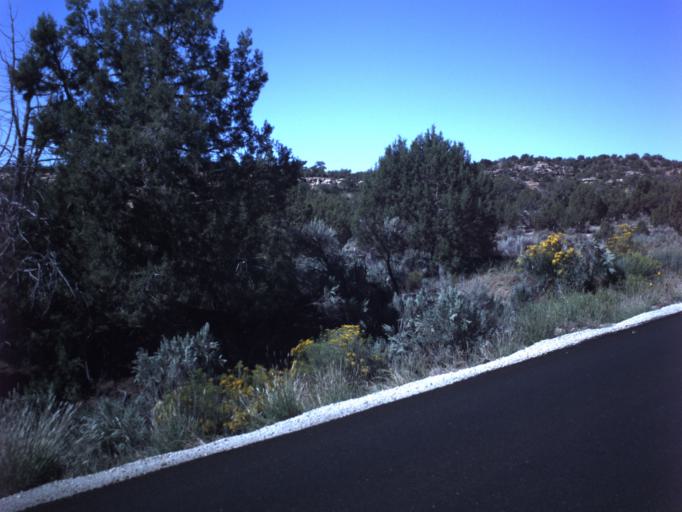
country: US
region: Utah
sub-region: San Juan County
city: Blanding
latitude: 37.5768
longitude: -109.5089
